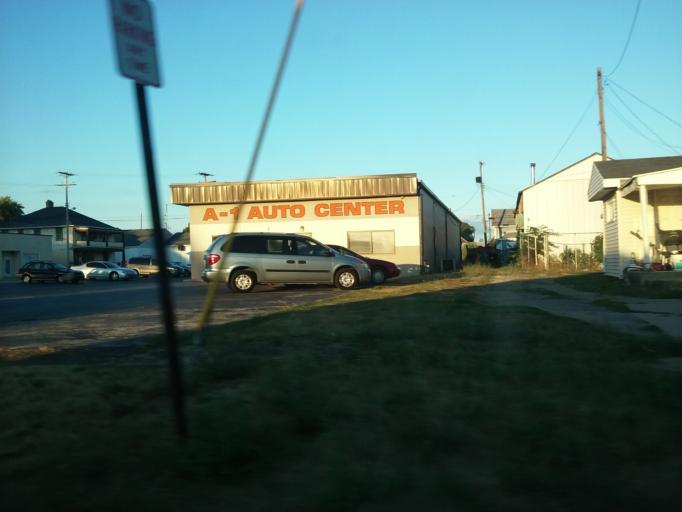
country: US
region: Ohio
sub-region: Hancock County
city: Findlay
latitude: 41.0453
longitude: -83.6519
